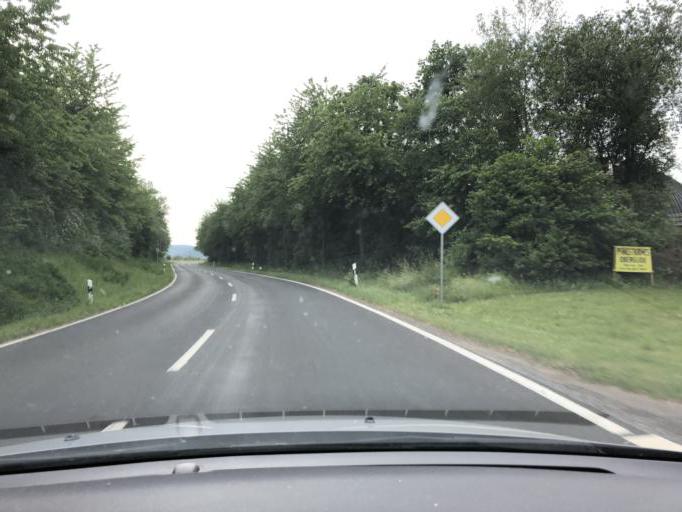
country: DE
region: Hesse
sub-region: Regierungsbezirk Kassel
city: Alheim
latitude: 51.0067
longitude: 9.6885
